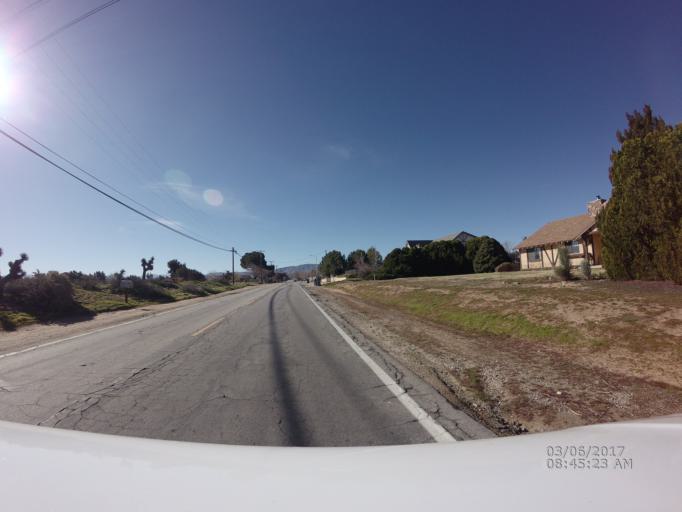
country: US
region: California
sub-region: Los Angeles County
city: Quartz Hill
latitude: 34.6721
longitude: -118.2102
